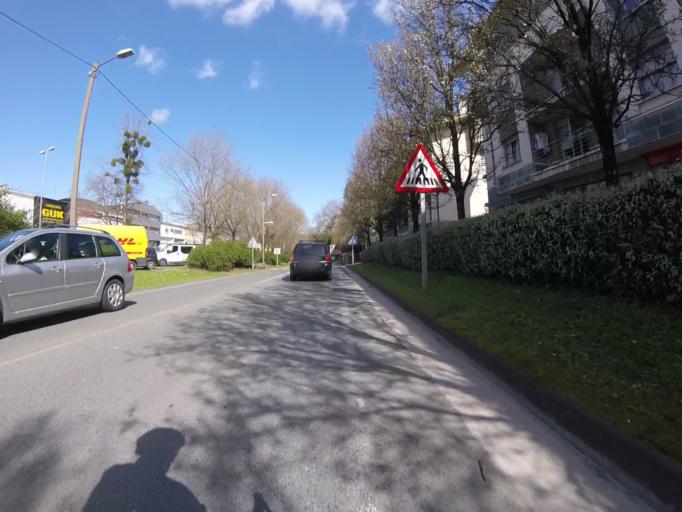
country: ES
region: Basque Country
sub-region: Provincia de Guipuzcoa
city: Astigarraga
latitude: 43.2807
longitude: -1.9506
